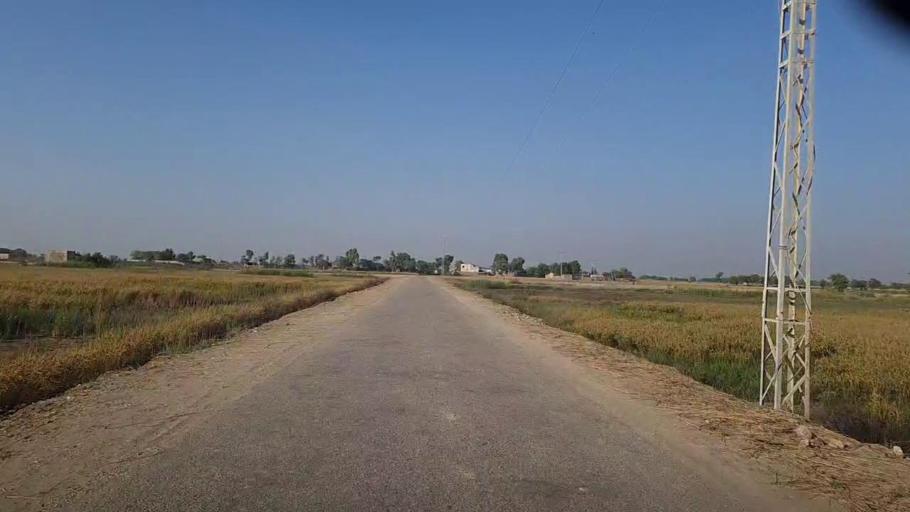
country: PK
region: Sindh
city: Tangwani
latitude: 28.2908
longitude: 68.9516
